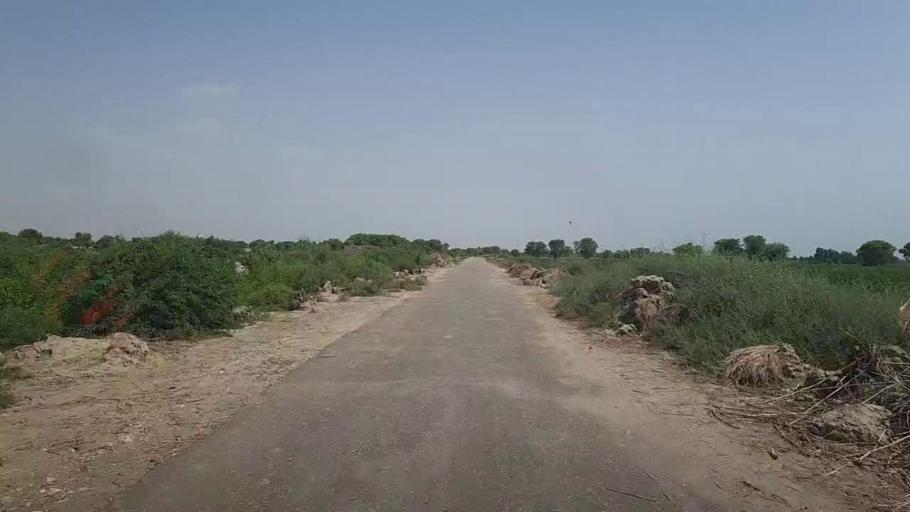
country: PK
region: Sindh
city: Pad Idan
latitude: 26.8108
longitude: 68.3295
